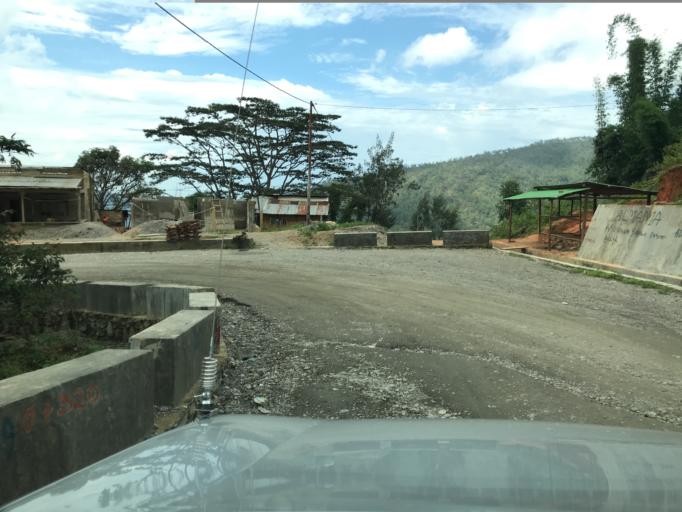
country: TL
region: Aileu
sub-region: Aileu Villa
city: Aileu
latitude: -8.6741
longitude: 125.5497
